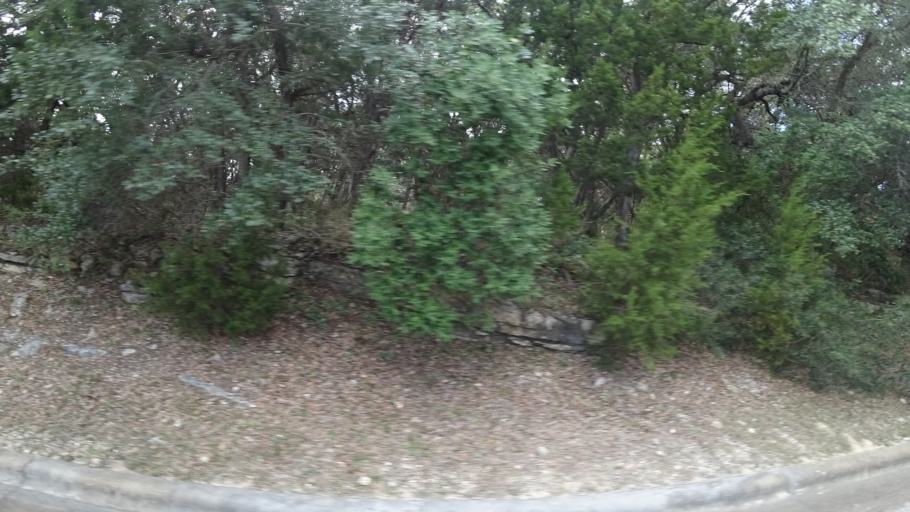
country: US
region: Texas
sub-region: Travis County
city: Barton Creek
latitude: 30.3156
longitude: -97.8747
